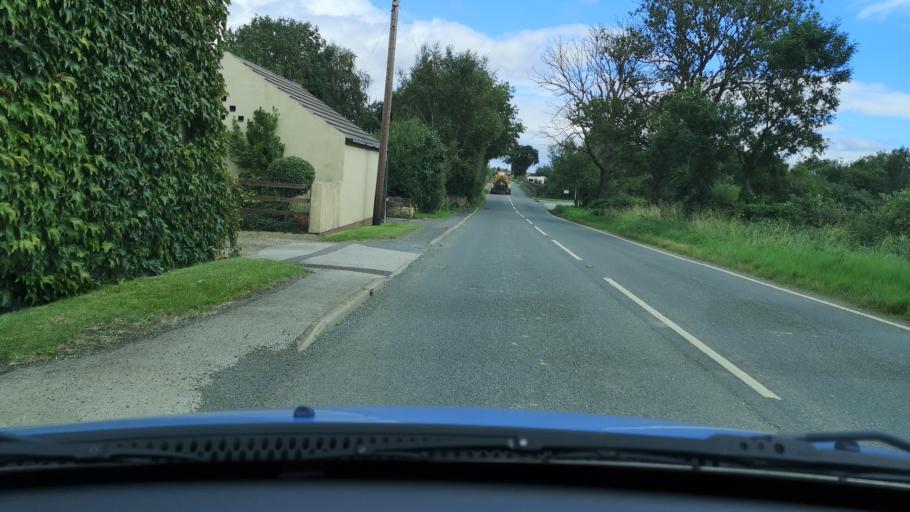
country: GB
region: England
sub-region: City and Borough of Wakefield
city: Badsworth
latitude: 53.6210
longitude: -1.3238
